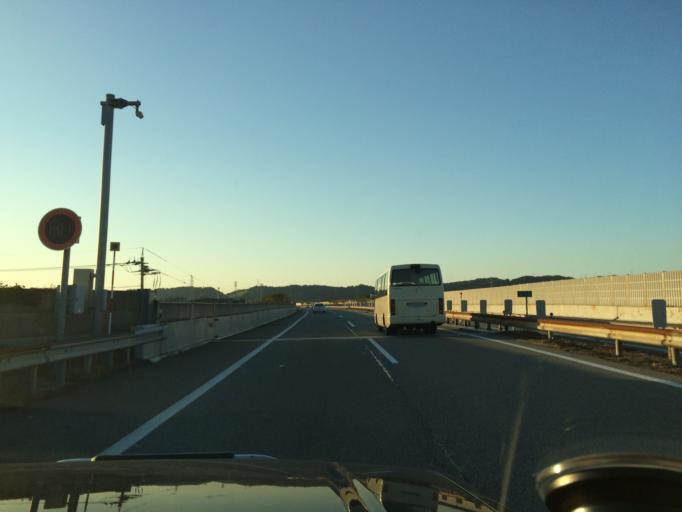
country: JP
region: Toyama
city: Toyama-shi
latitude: 36.6709
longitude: 137.1781
